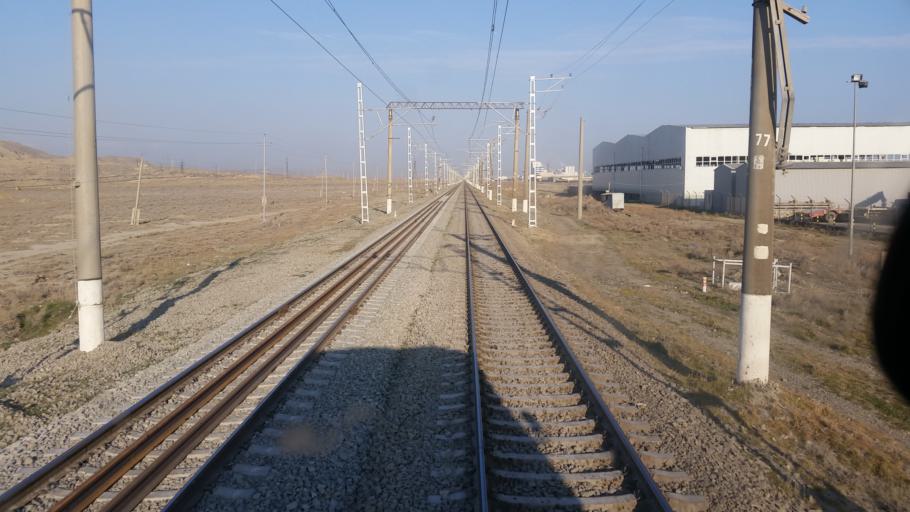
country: AZ
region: Baki
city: Korgoz
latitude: 40.2585
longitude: 49.6294
